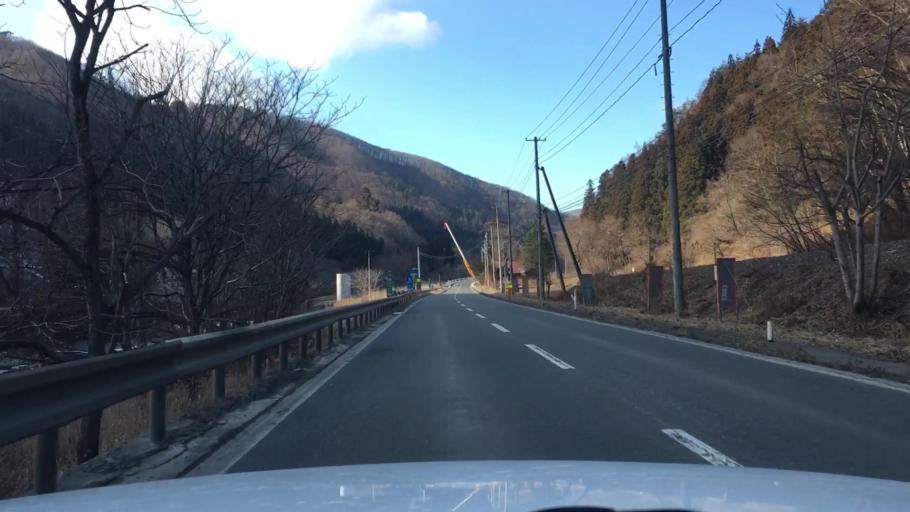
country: JP
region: Iwate
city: Miyako
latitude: 39.6094
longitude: 141.6342
